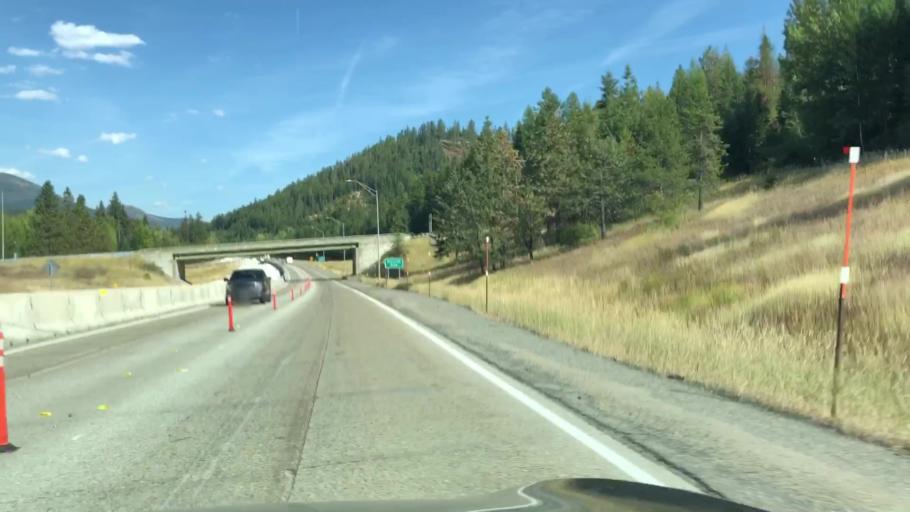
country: US
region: Idaho
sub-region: Shoshone County
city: Wallace
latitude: 47.4683
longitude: -115.7873
